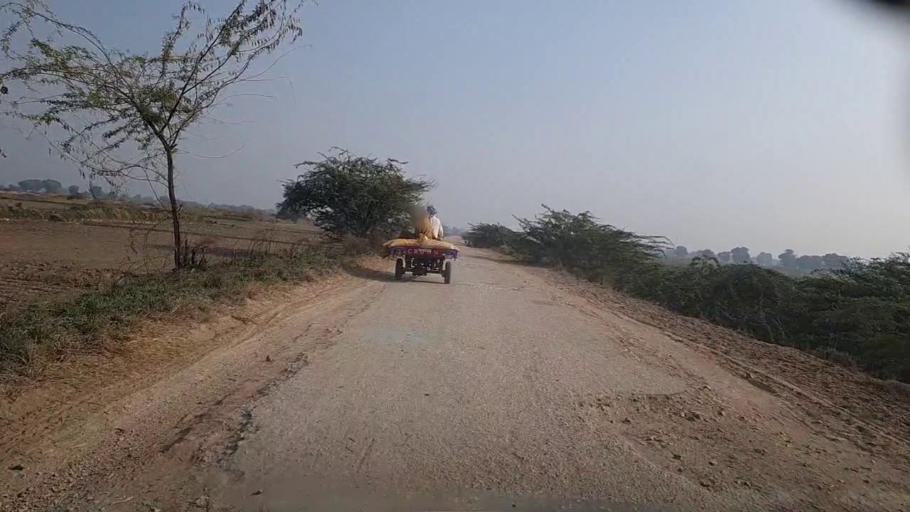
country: PK
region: Sindh
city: Setharja Old
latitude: 27.0648
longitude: 68.4531
